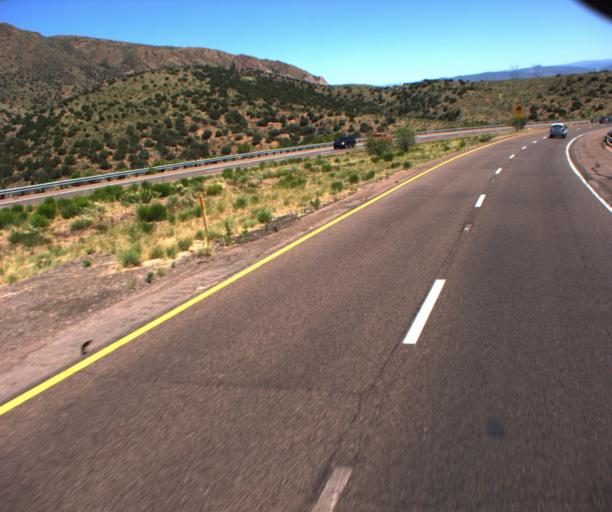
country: US
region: Arizona
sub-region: Gila County
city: Tonto Basin
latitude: 33.9943
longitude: -111.3688
